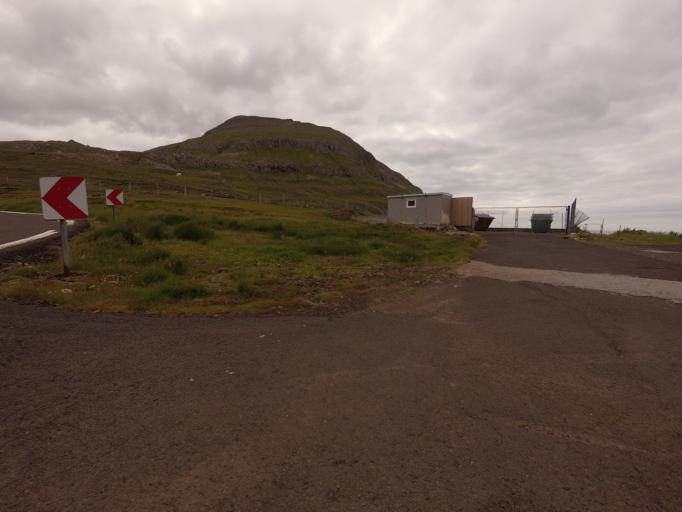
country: FO
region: Suduroy
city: Tvoroyri
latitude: 61.5190
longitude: -6.8897
